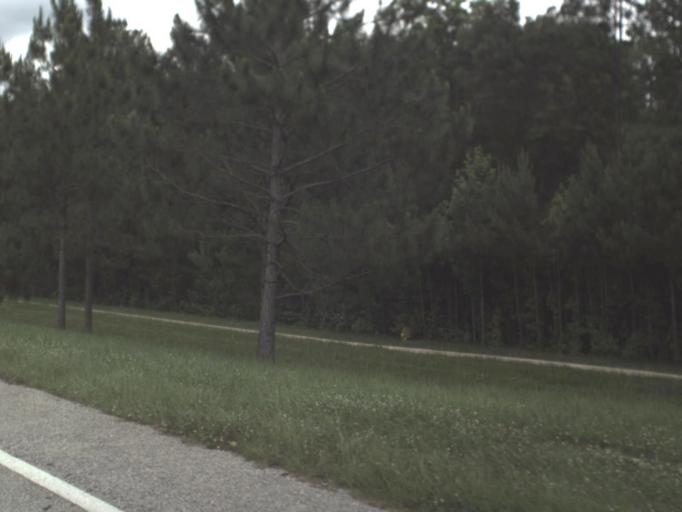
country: US
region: Florida
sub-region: Duval County
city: Jacksonville
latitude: 30.4685
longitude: -81.6671
